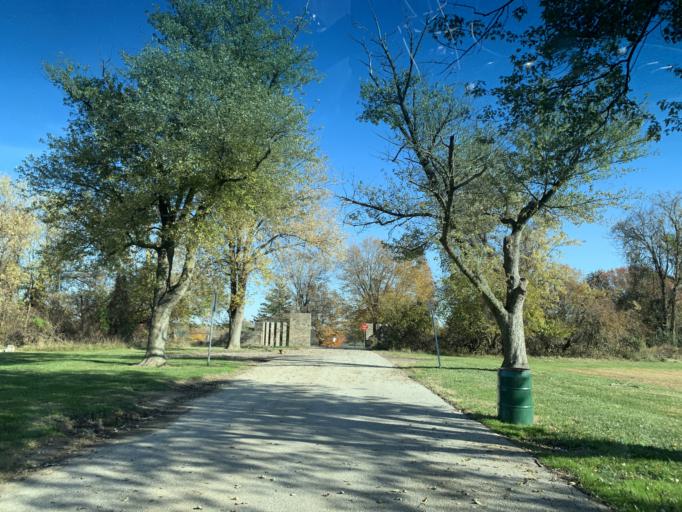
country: US
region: Maryland
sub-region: Baltimore County
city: Timonium
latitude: 39.4576
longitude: -76.6226
